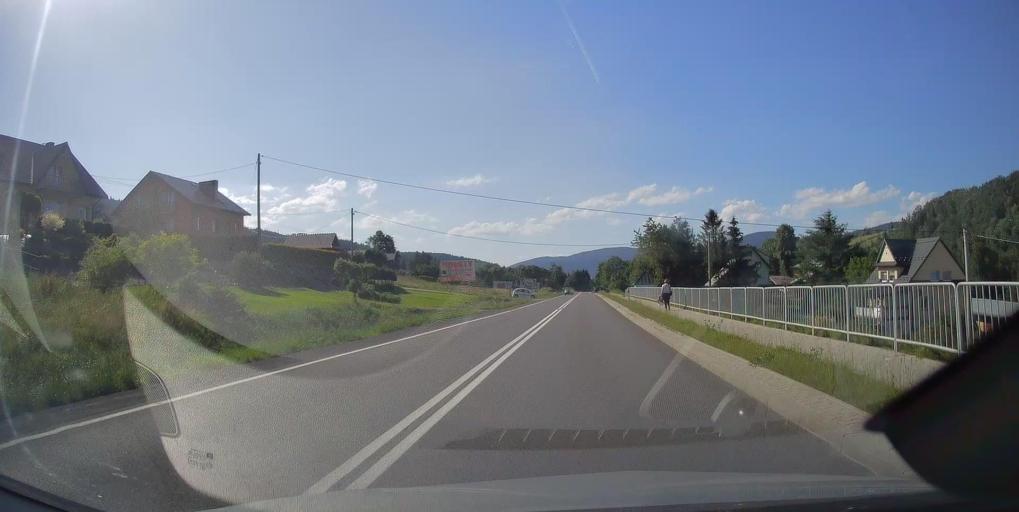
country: PL
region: Lesser Poland Voivodeship
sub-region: Powiat nowosadecki
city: Labowa
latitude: 49.4984
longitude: 20.9024
